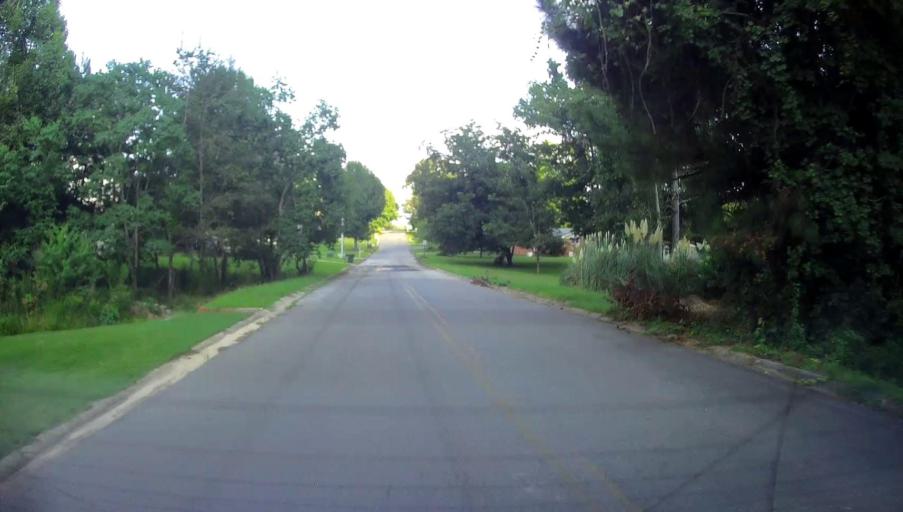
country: US
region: Georgia
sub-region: Houston County
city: Warner Robins
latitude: 32.5851
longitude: -83.6484
